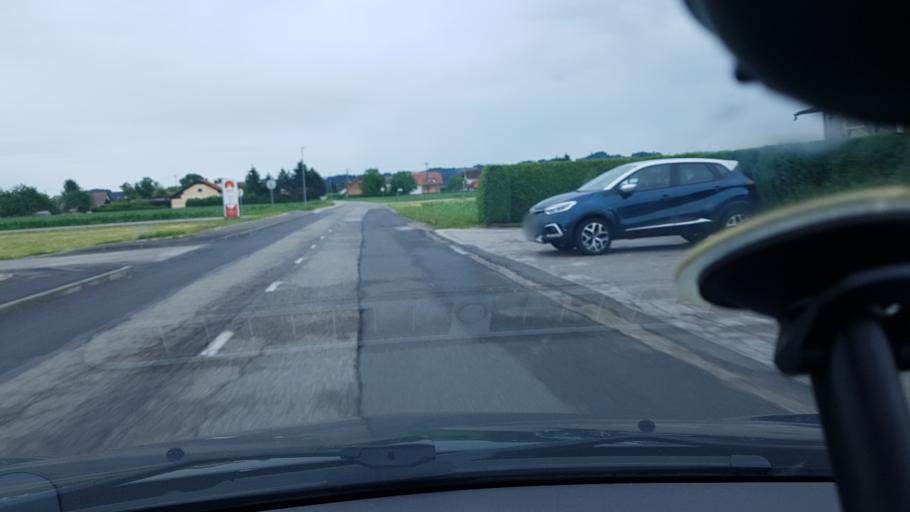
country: SI
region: Ptuj
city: Ptuj
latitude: 46.3867
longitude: 15.8735
